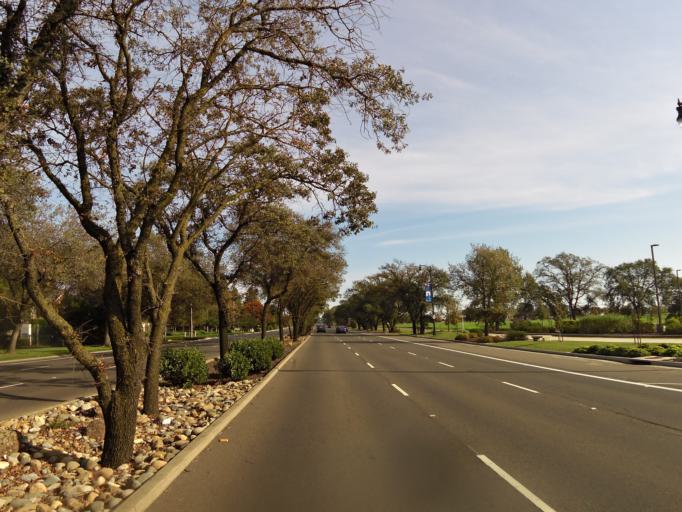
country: US
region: California
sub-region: Sacramento County
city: Laguna
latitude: 38.4090
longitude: -121.4001
